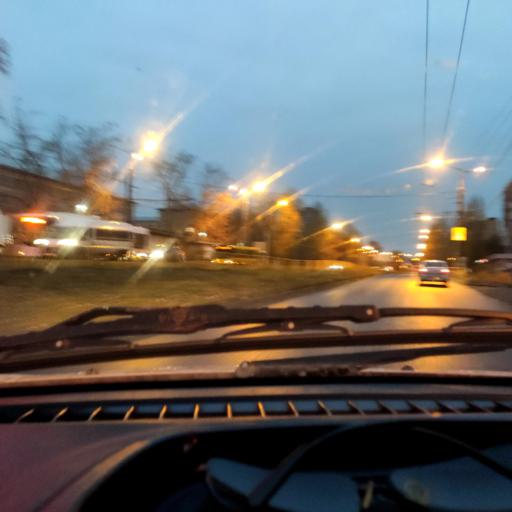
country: RU
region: Samara
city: Zhigulevsk
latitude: 53.4818
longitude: 49.4742
